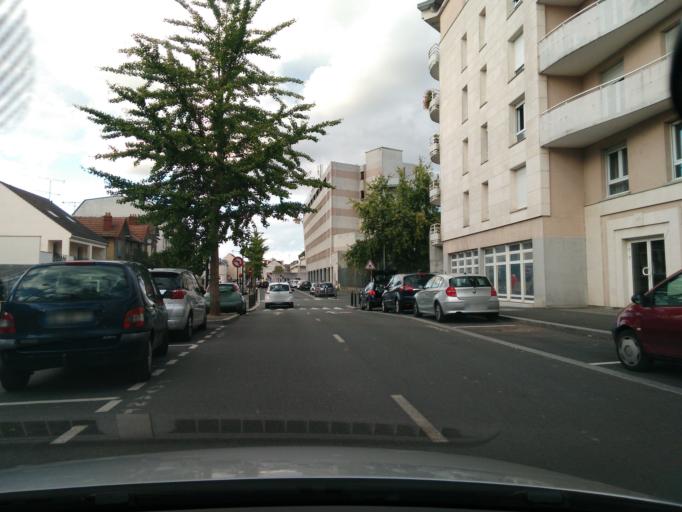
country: FR
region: Ile-de-France
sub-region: Departement de Seine-et-Marne
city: Meaux
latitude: 48.9548
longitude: 2.8857
